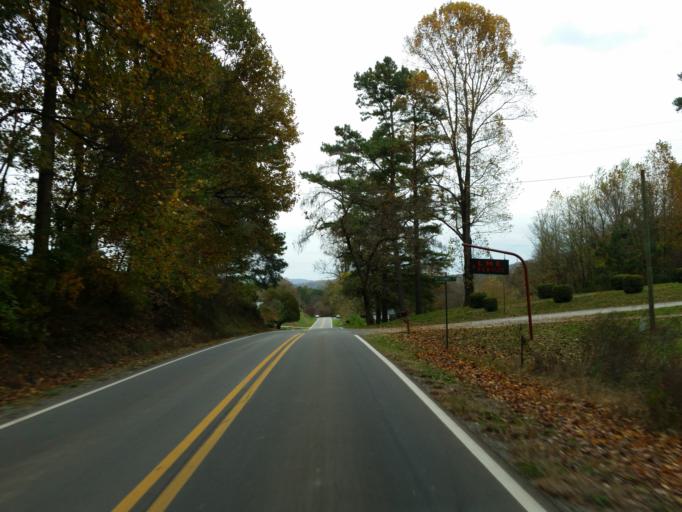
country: US
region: Georgia
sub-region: Gilmer County
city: Ellijay
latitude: 34.6498
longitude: -84.3497
